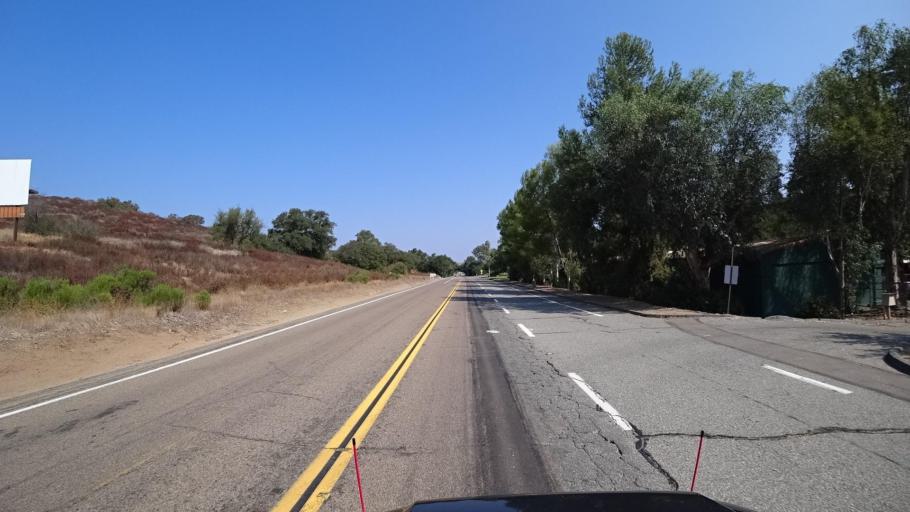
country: US
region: California
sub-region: San Diego County
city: Hidden Meadows
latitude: 33.2366
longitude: -117.1466
